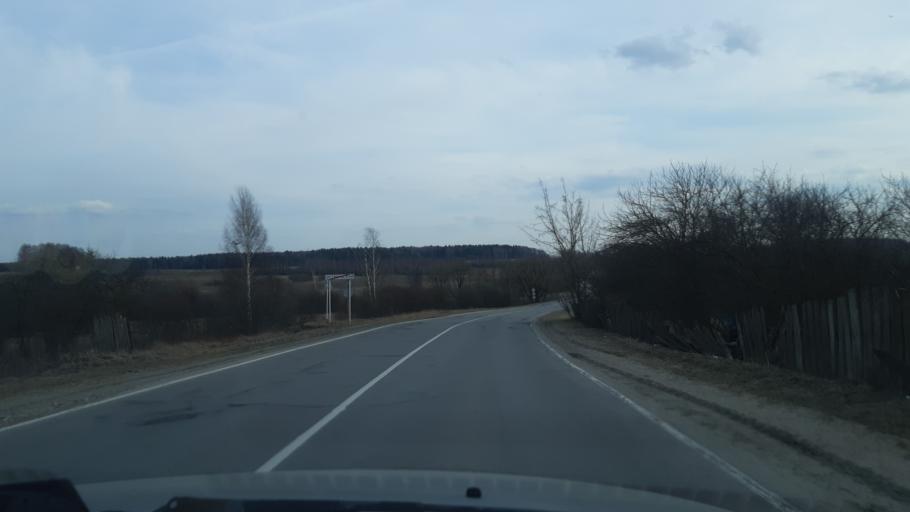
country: RU
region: Vladimir
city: Luknovo
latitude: 56.2139
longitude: 42.0306
